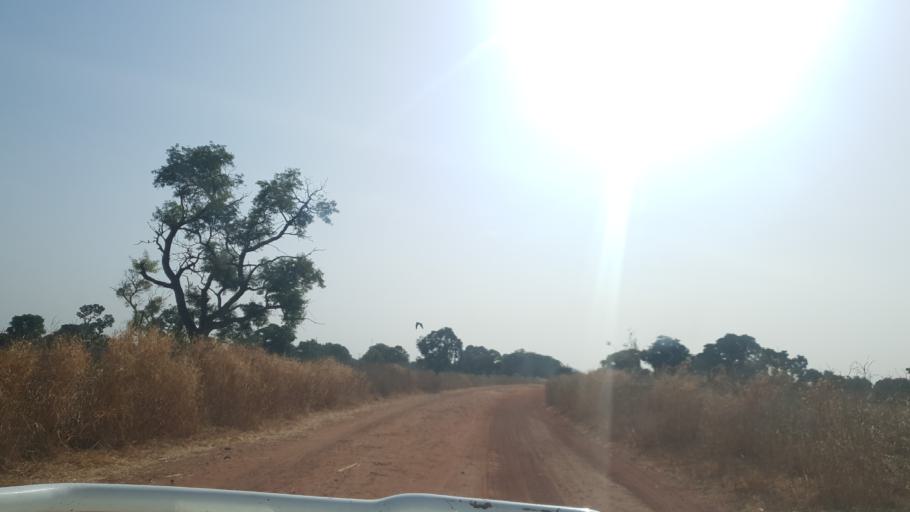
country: ML
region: Koulikoro
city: Dioila
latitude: 12.7061
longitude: -6.7709
